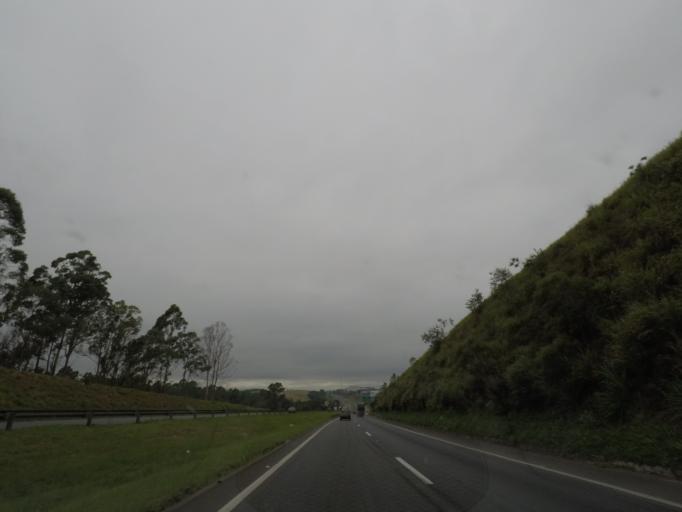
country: BR
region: Sao Paulo
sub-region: Jarinu
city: Jarinu
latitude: -23.0360
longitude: -46.7126
